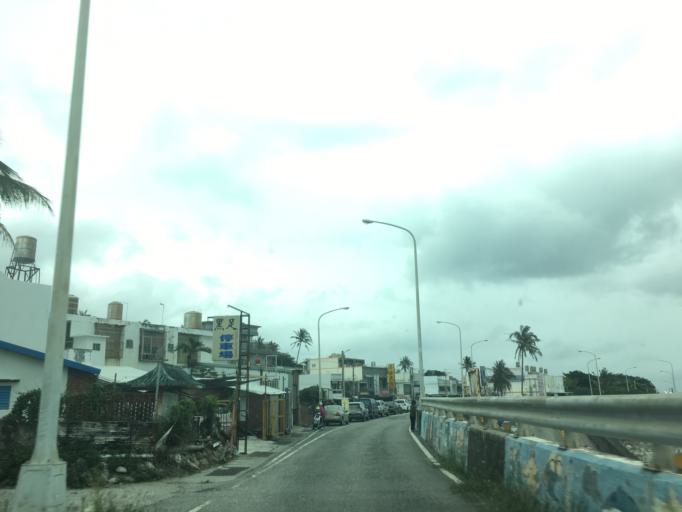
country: TW
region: Taiwan
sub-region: Taitung
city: Taitung
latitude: 22.7925
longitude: 121.1891
